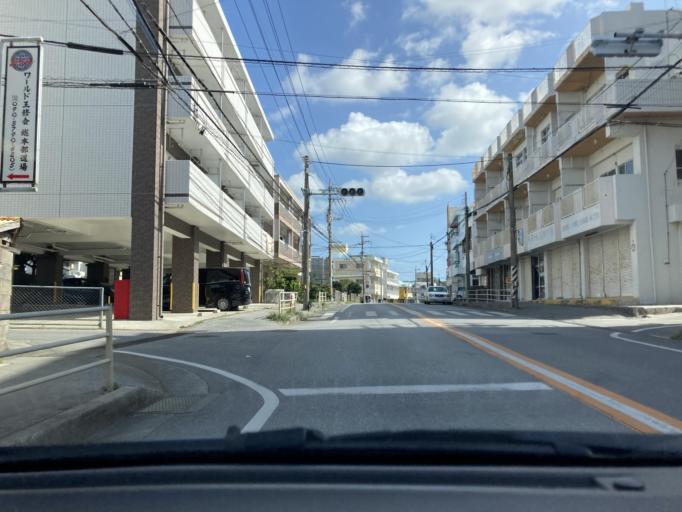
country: JP
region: Okinawa
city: Tomigusuku
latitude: 26.1853
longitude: 127.6814
